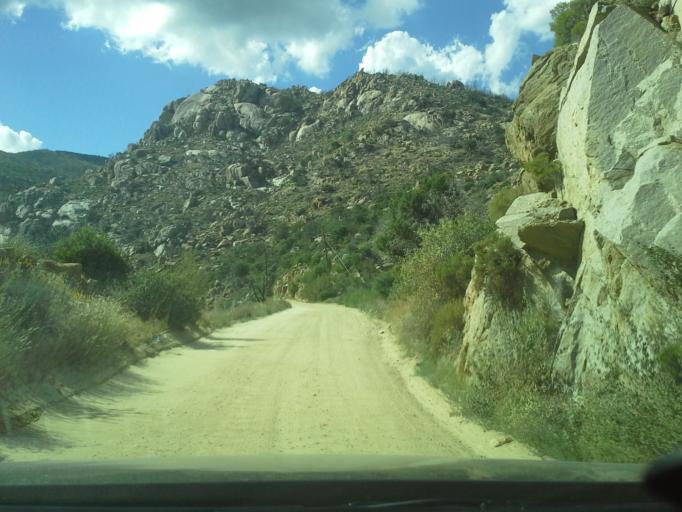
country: US
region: Arizona
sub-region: Yavapai County
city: Mayer
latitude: 34.2135
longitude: -112.3177
